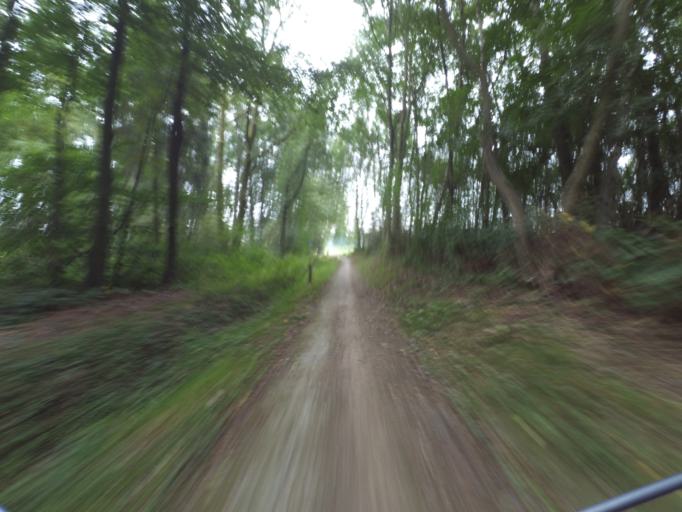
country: NL
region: Overijssel
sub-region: Gemeente Losser
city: Losser
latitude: 52.3036
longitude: 7.0027
